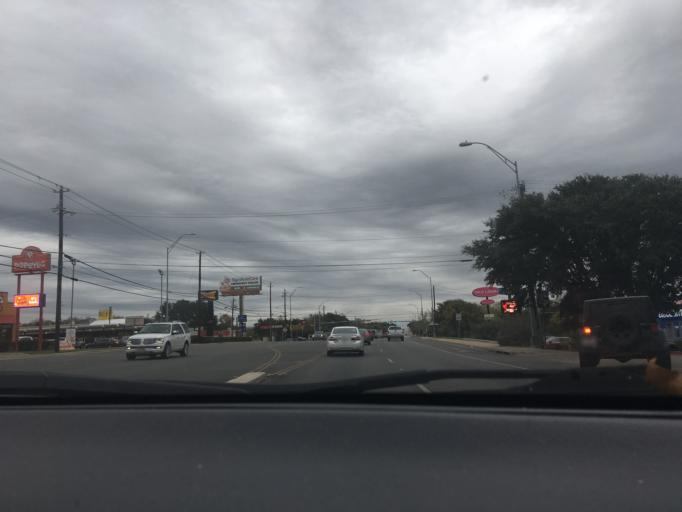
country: US
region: Texas
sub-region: Travis County
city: Manchaca
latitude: 30.1744
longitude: -97.8234
